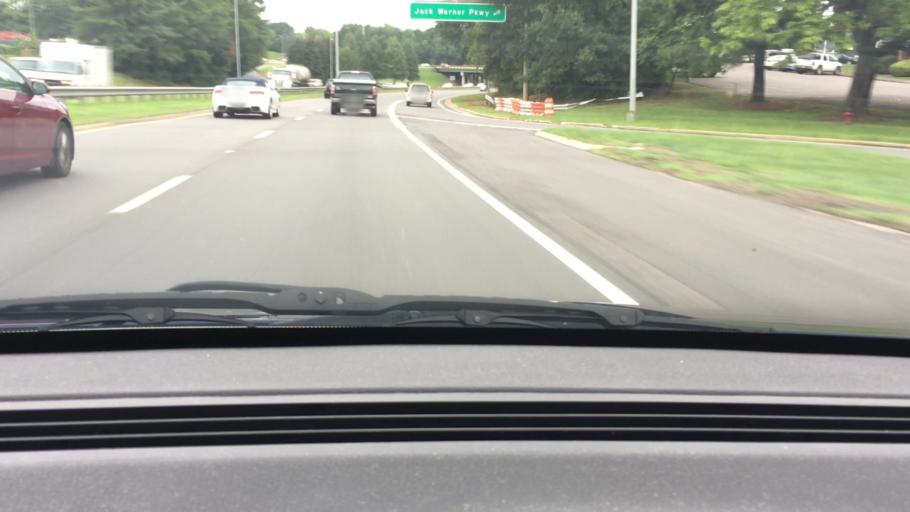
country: US
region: Alabama
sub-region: Tuscaloosa County
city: Tuscaloosa
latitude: 33.2171
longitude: -87.5301
